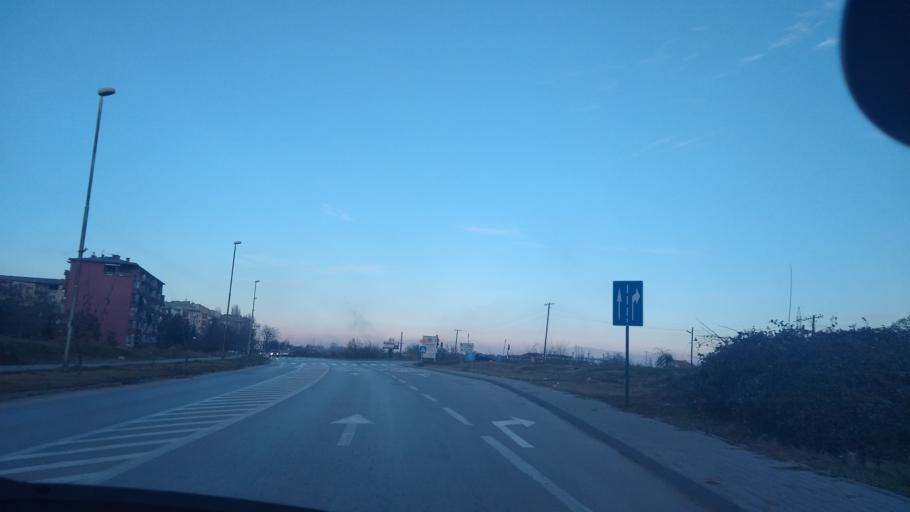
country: MK
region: Bitola
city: Bitola
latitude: 41.0258
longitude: 21.3449
